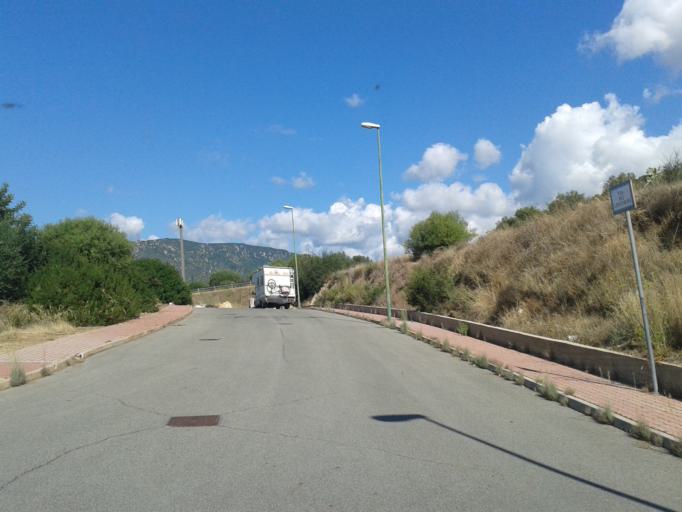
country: IT
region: Sardinia
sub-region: Provincia di Cagliari
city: Villasimius
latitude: 39.1515
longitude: 9.5199
